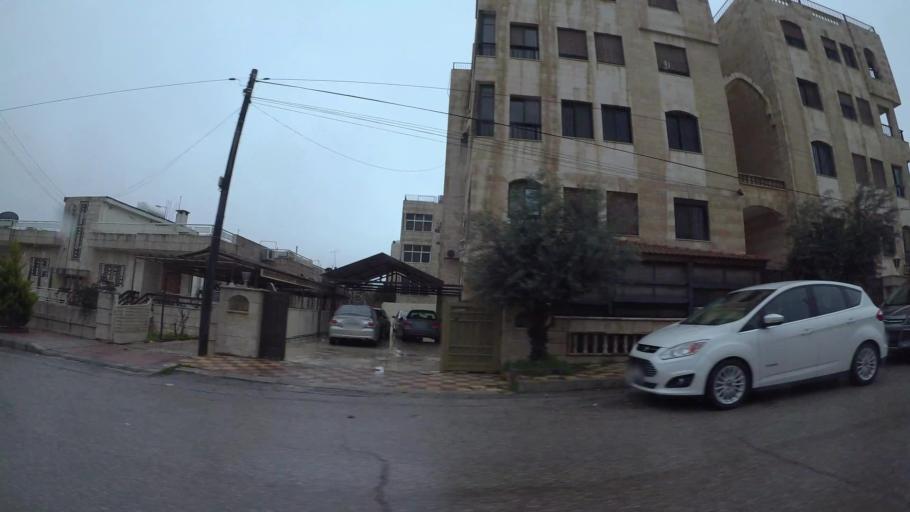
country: JO
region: Amman
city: Al Jubayhah
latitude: 32.0293
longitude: 35.8531
